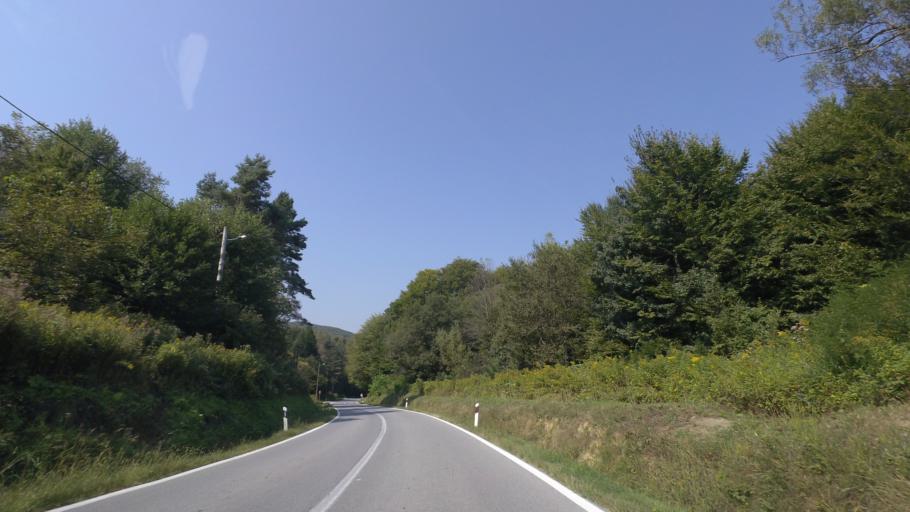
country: HR
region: Bjelovarsko-Bilogorska
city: Sirac
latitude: 45.4663
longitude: 17.3989
